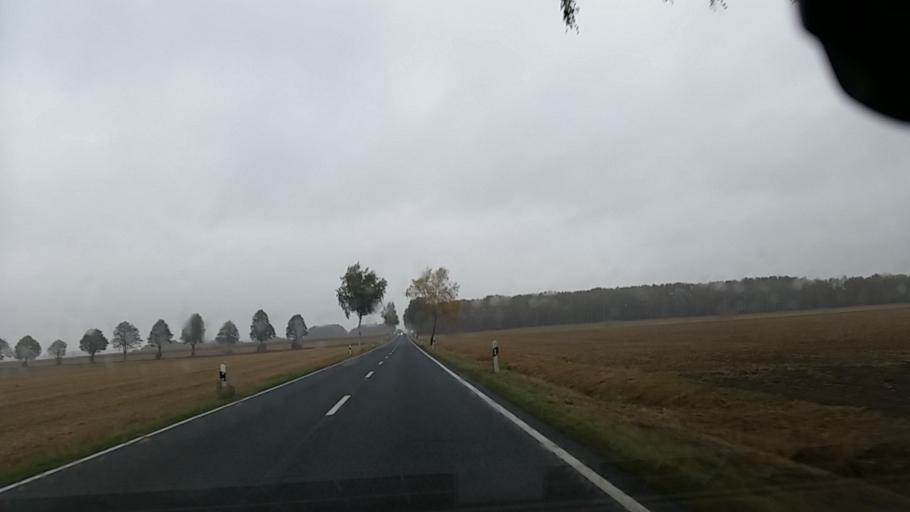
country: DE
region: Lower Saxony
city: Wittingen
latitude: 52.7373
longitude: 10.7362
